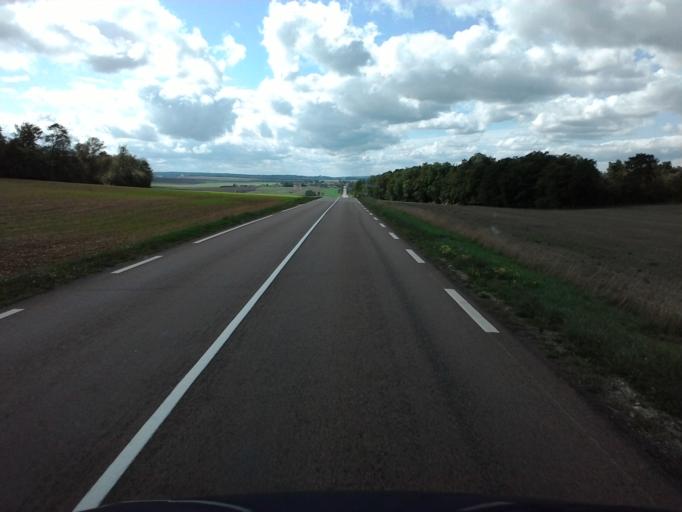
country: FR
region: Lorraine
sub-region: Departement de Meurthe-et-Moselle
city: Colombey-les-Belles
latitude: 48.4970
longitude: 5.8697
